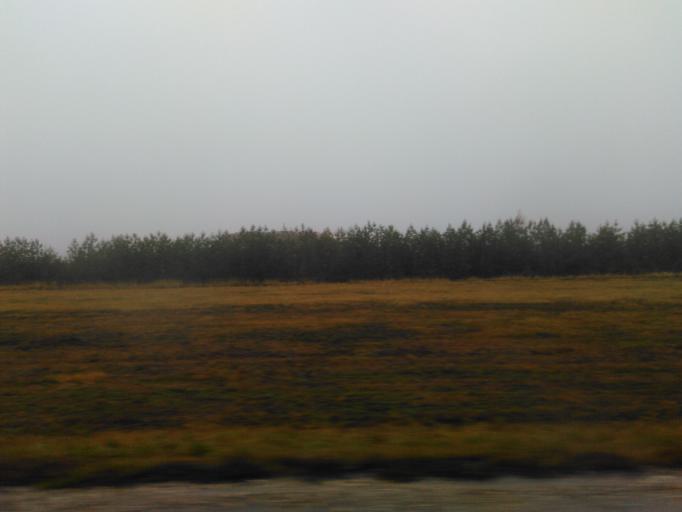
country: RU
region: Tatarstan
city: Sviyazhsk
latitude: 55.7377
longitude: 48.7841
